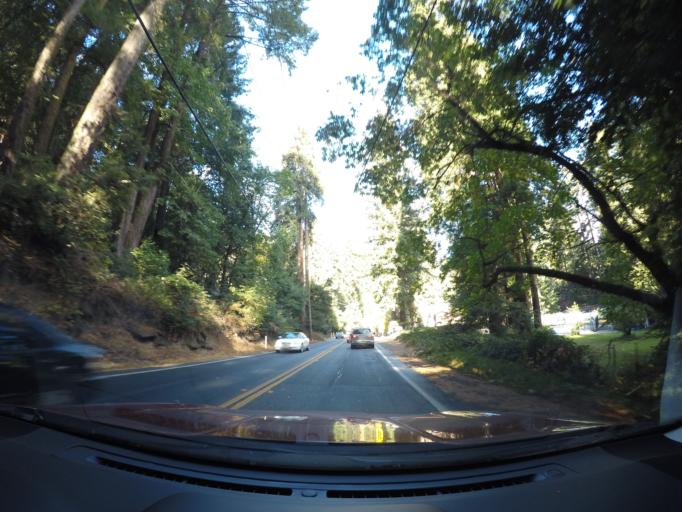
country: US
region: California
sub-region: Santa Cruz County
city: Ben Lomond
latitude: 37.0847
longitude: -122.0893
